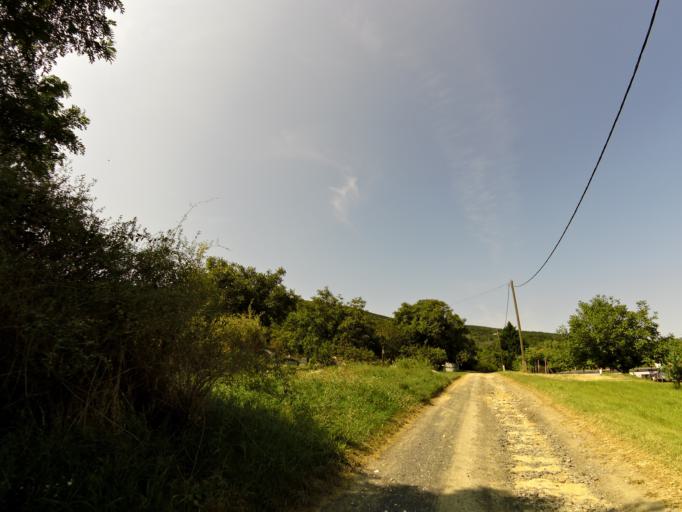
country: HU
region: Zala
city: Vonyarcvashegy
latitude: 46.8114
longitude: 17.3764
